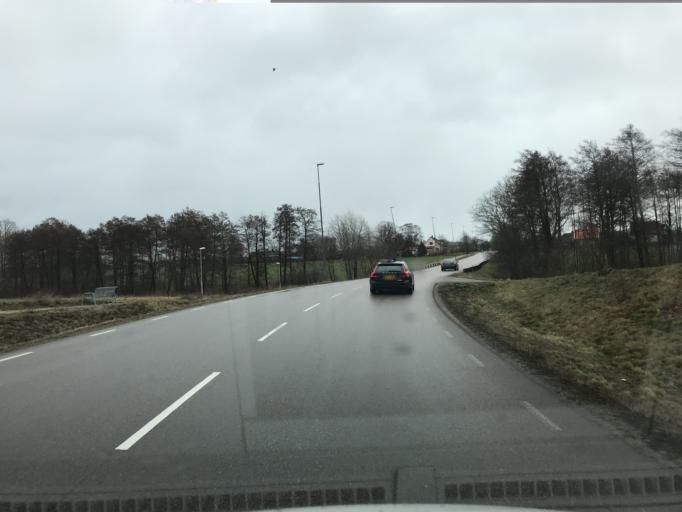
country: SE
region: Skane
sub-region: Klippans Kommun
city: Klippan
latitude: 56.1212
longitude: 13.1705
